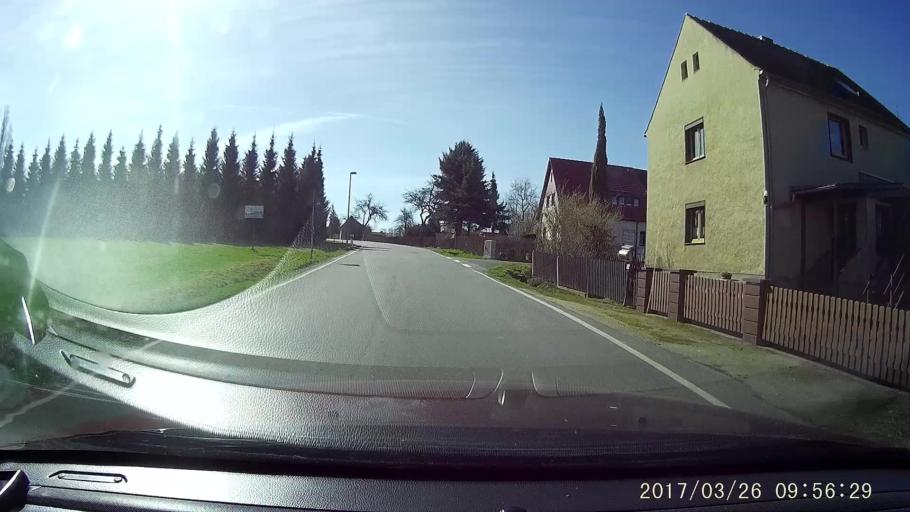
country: DE
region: Saxony
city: Sohland am Rotstein
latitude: 51.0891
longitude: 14.7365
